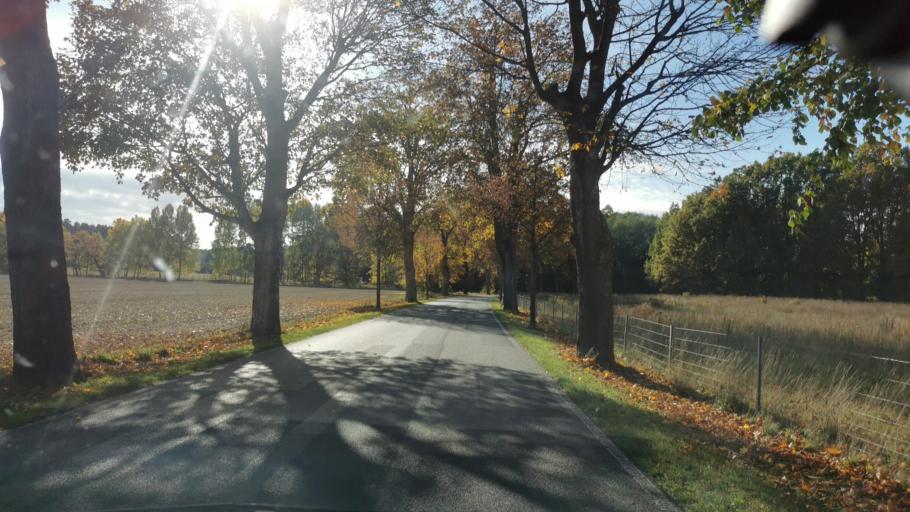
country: DE
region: Brandenburg
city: Eberswalde
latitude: 52.7553
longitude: 13.7944
